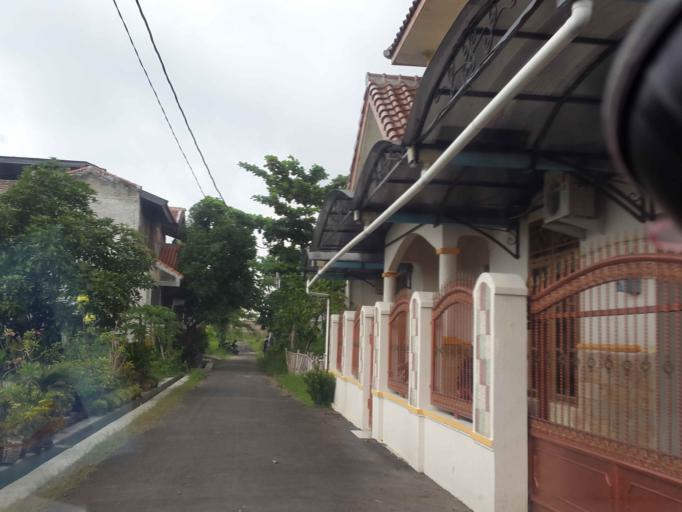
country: ID
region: Central Java
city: Tegal
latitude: -6.8815
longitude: 109.1436
